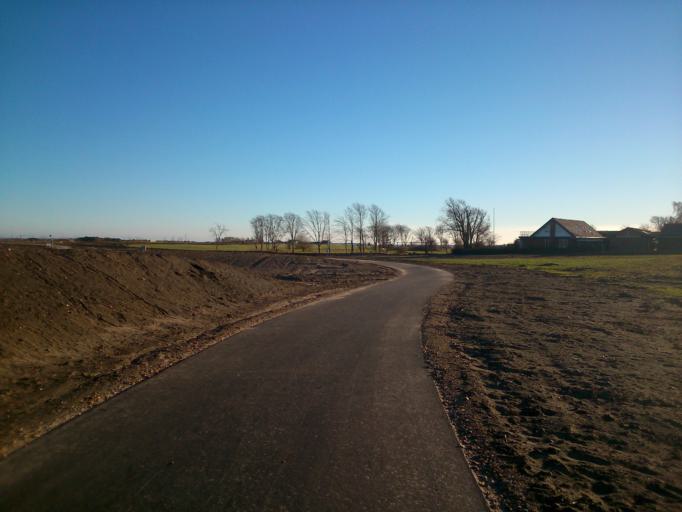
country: DK
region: Central Jutland
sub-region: Ringkobing-Skjern Kommune
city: Ringkobing
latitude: 56.0736
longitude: 8.2799
